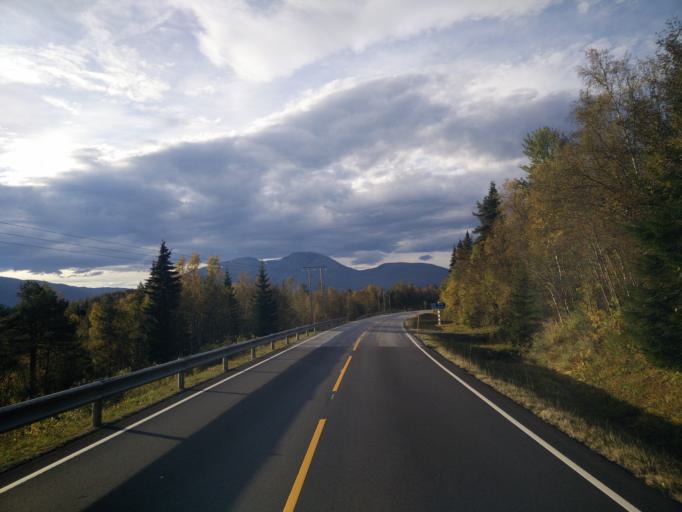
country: NO
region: More og Romsdal
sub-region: Gjemnes
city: Batnfjordsora
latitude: 62.8263
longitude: 7.6047
